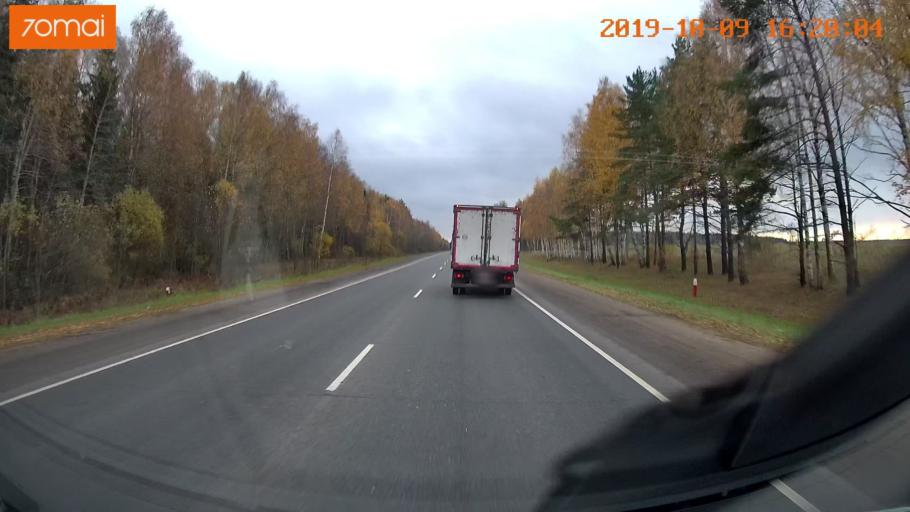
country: RU
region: Kostroma
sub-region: Kostromskoy Rayon
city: Kostroma
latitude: 57.7113
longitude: 40.8931
